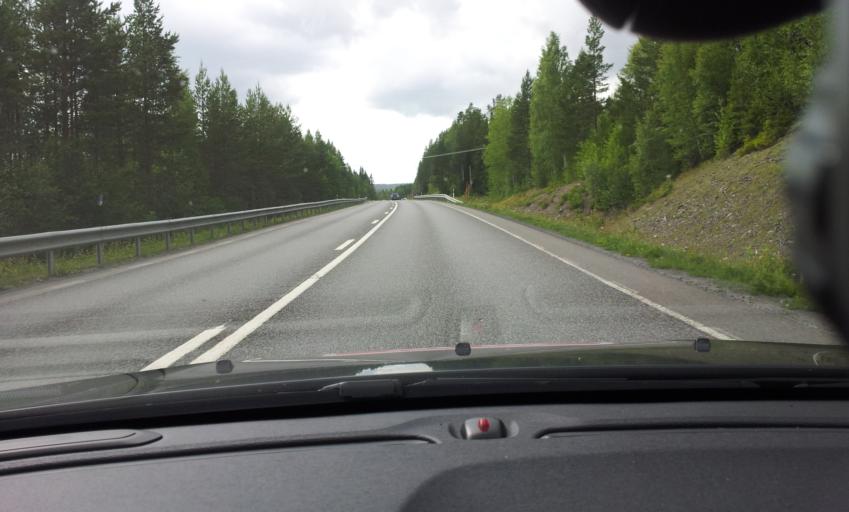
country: SE
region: Jaemtland
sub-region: Krokoms Kommun
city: Valla
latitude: 63.3370
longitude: 14.0039
